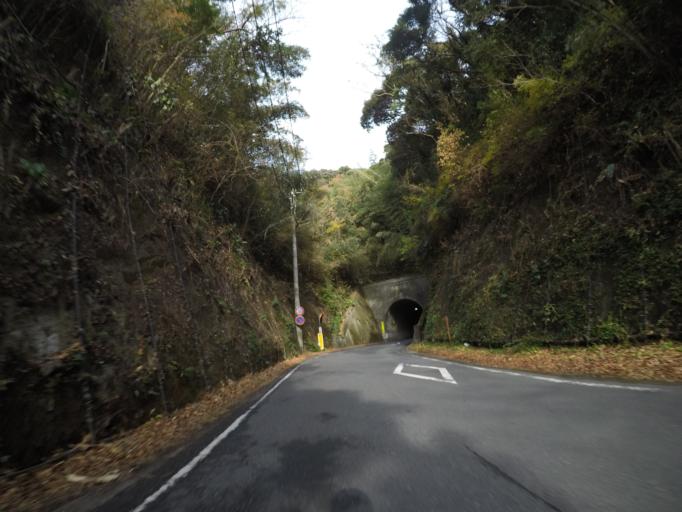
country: JP
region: Shizuoka
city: Heda
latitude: 34.7958
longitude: 138.7637
